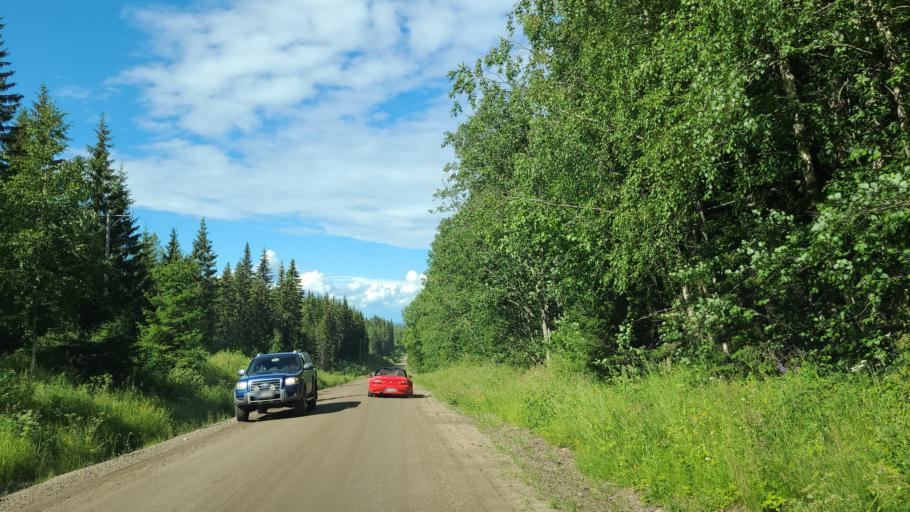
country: FI
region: Northern Savo
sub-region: Koillis-Savo
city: Kaavi
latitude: 62.9462
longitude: 28.7646
